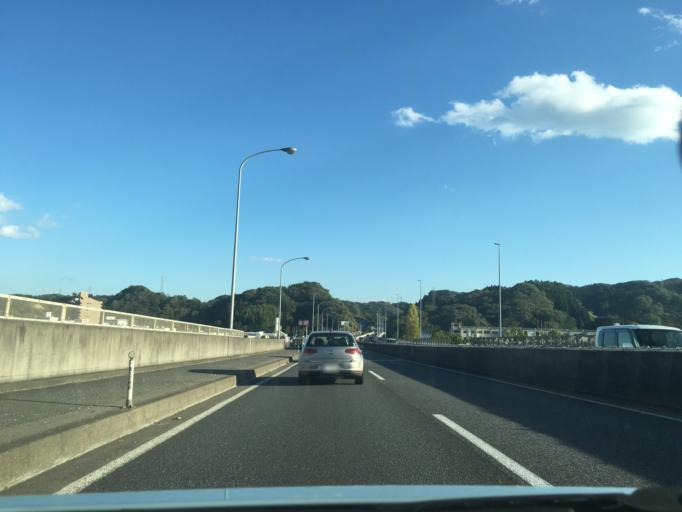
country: JP
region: Fukushima
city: Iwaki
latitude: 37.0494
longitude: 140.8677
